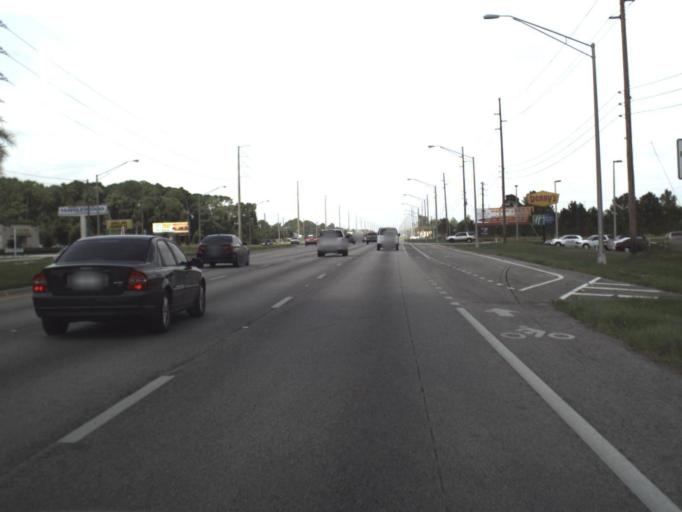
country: US
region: Florida
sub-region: Highlands County
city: Sebring
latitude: 27.5226
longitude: -81.4978
